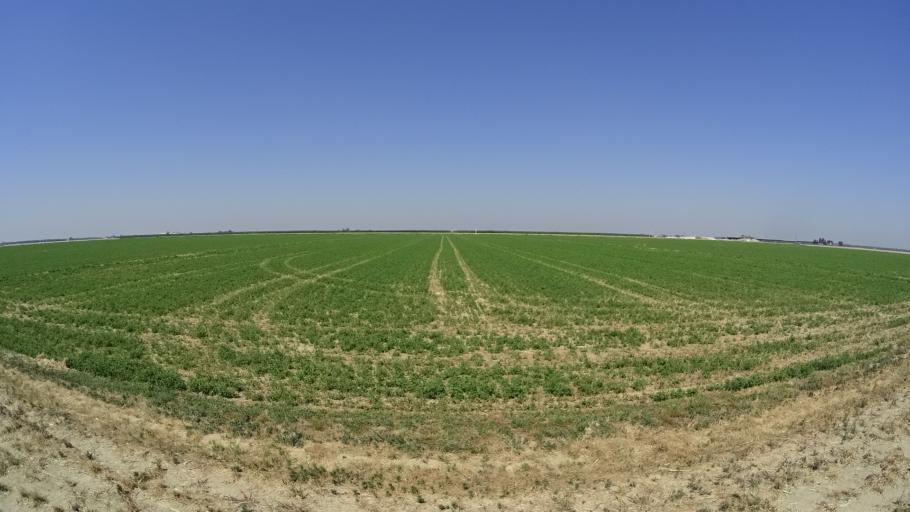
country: US
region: California
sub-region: Tulare County
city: Goshen
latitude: 36.3904
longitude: -119.5289
